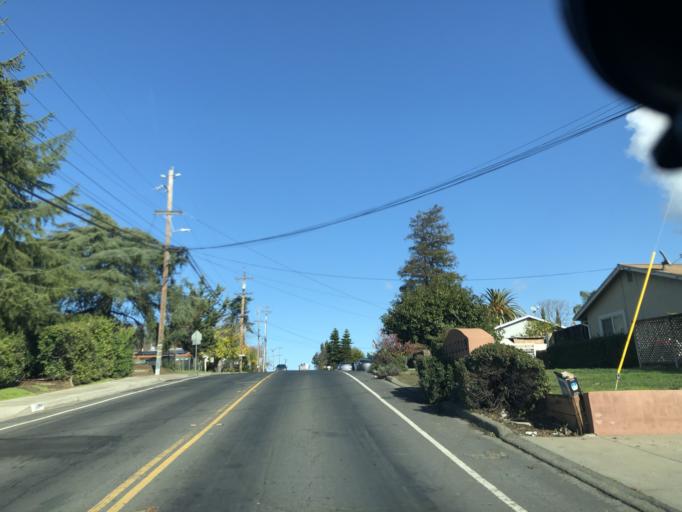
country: US
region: California
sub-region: Contra Costa County
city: Vine Hill
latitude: 38.0087
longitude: -122.0900
